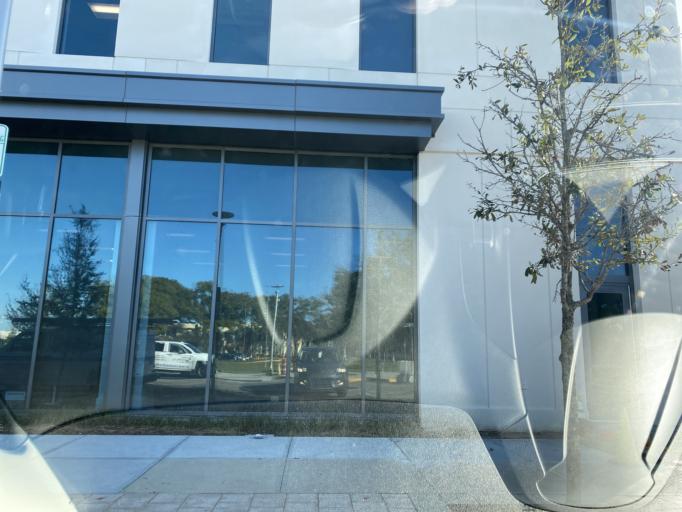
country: US
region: Florida
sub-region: Orange County
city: Orlando
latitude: 28.5470
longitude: -81.3870
